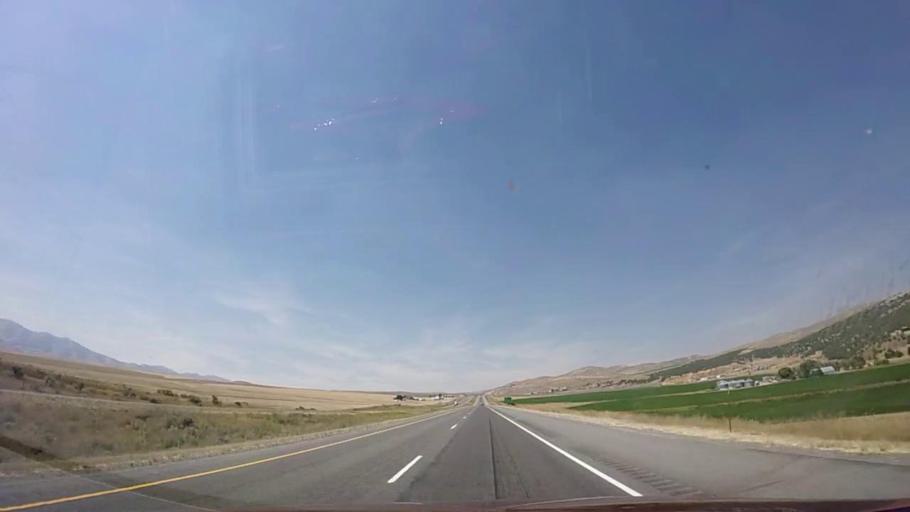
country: US
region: Idaho
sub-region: Power County
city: American Falls
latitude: 42.1614
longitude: -112.9930
